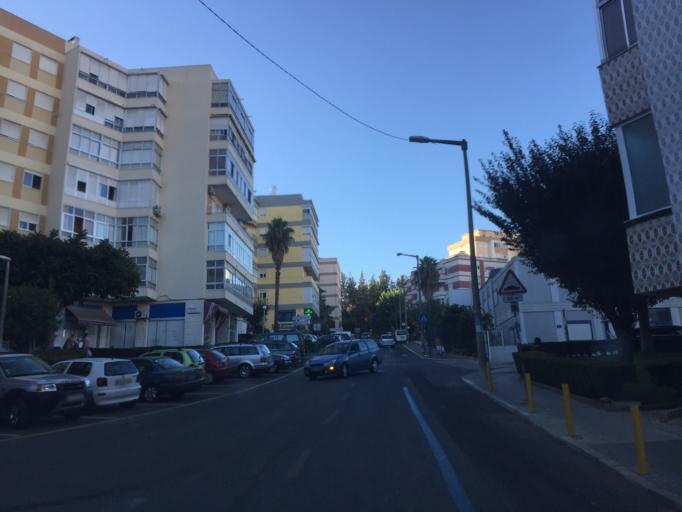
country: PT
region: Lisbon
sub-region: Odivelas
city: Povoa de Santo Adriao
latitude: 38.7986
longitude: -9.1634
